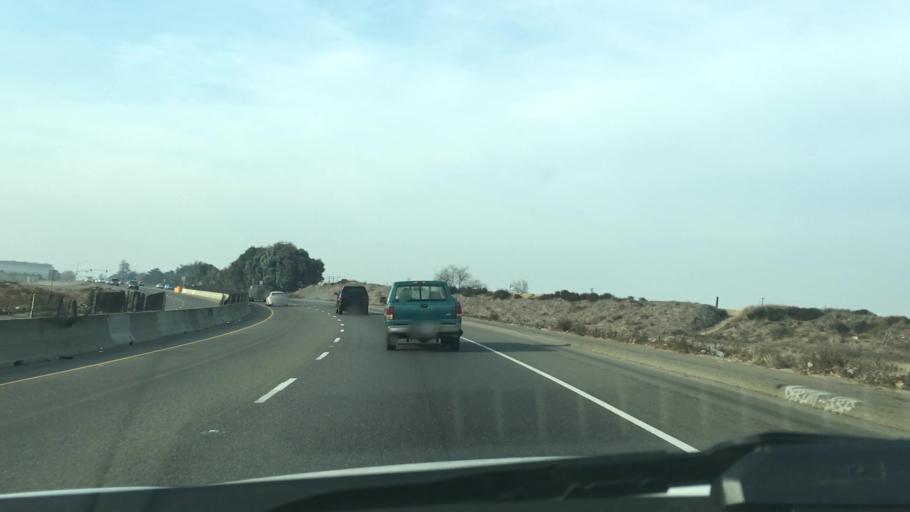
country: US
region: California
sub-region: Stanislaus County
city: Ceres
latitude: 37.6208
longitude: -120.9395
